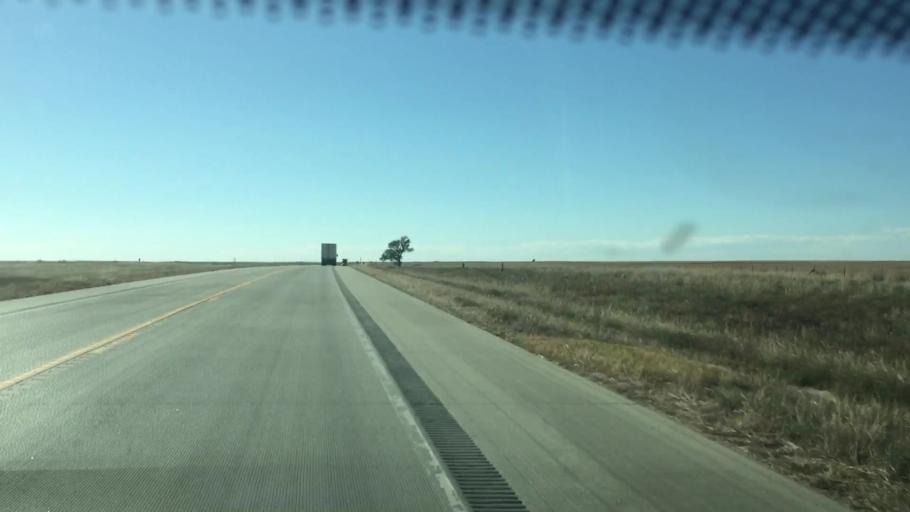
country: US
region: Colorado
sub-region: Kiowa County
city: Eads
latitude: 38.7639
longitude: -102.8239
